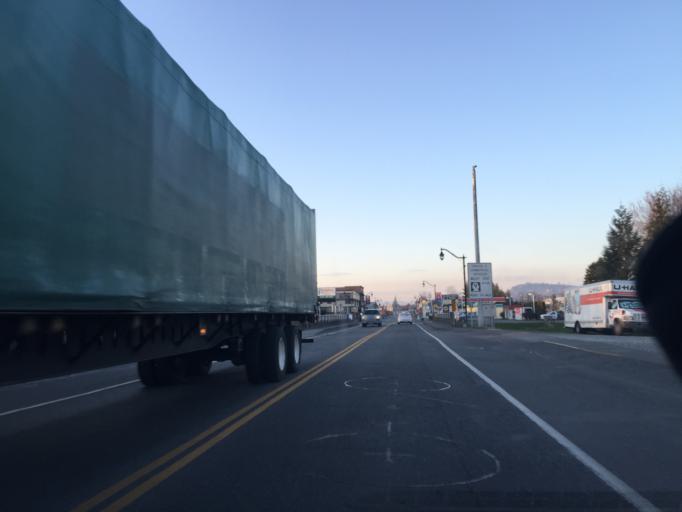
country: US
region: Washington
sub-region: Whatcom County
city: Sumas
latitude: 48.9968
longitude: -122.2650
